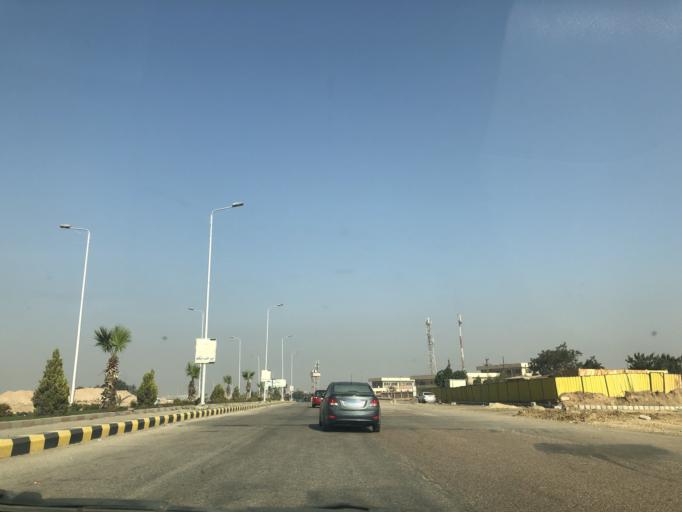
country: EG
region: Al Jizah
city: Madinat Sittah Uktubar
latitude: 29.9527
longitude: 31.0743
